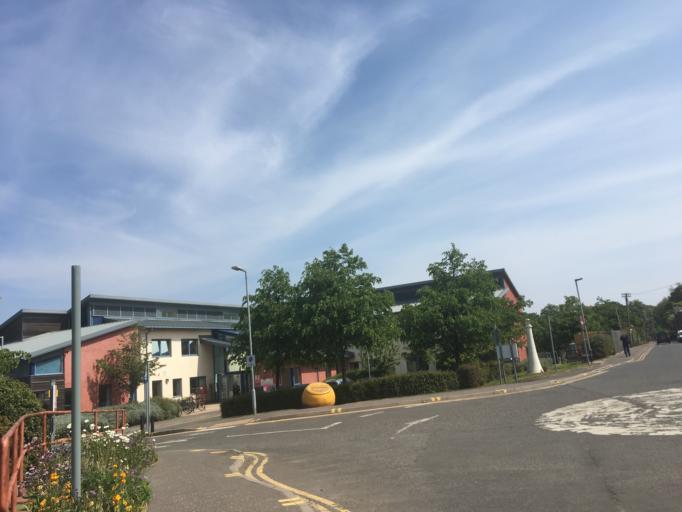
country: GB
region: Scotland
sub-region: Edinburgh
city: Edinburgh
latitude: 55.9275
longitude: -3.2186
